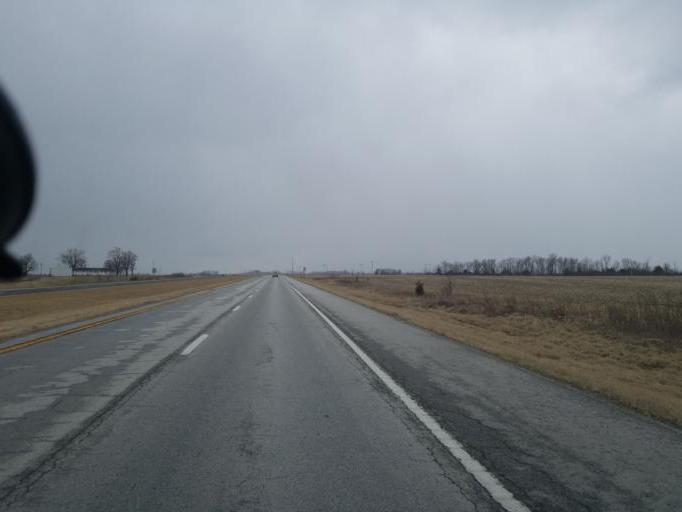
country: US
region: Missouri
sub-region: Macon County
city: La Plata
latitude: 39.8860
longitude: -92.4719
